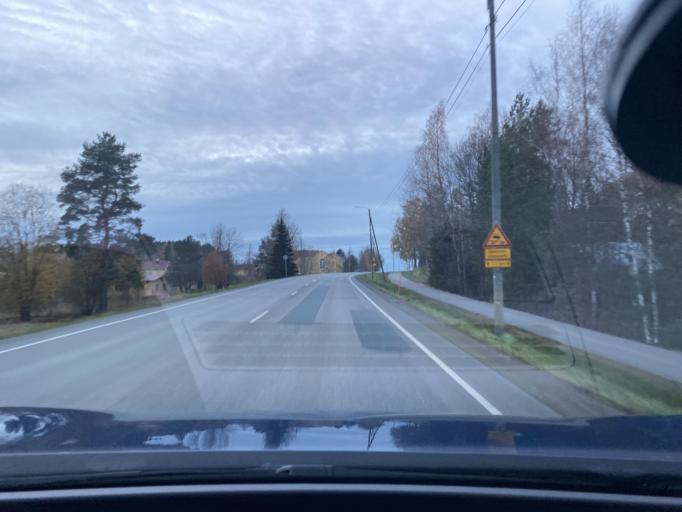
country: FI
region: Uusimaa
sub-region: Helsinki
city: Saukkola
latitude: 60.3854
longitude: 23.9185
